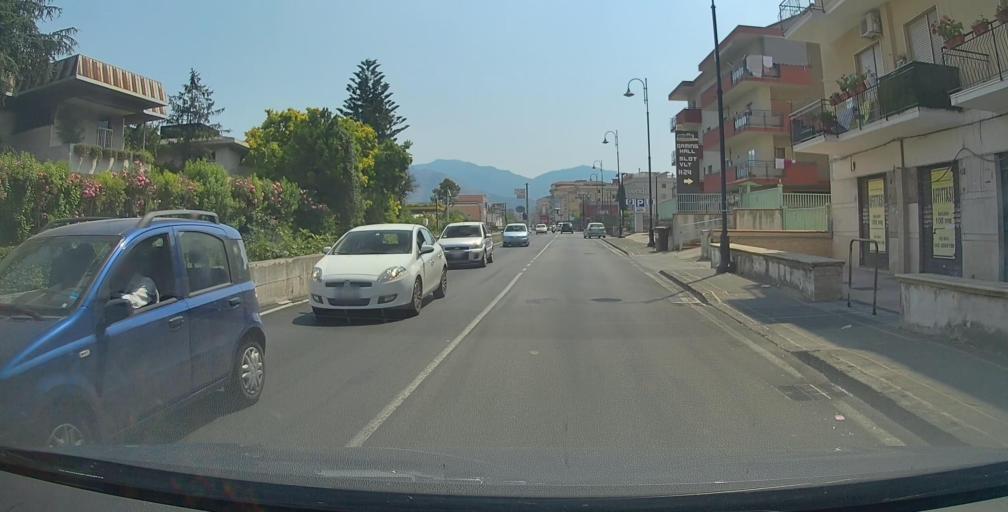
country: IT
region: Campania
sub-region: Provincia di Salerno
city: Nocera Inferiore
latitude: 40.7410
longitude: 14.6498
